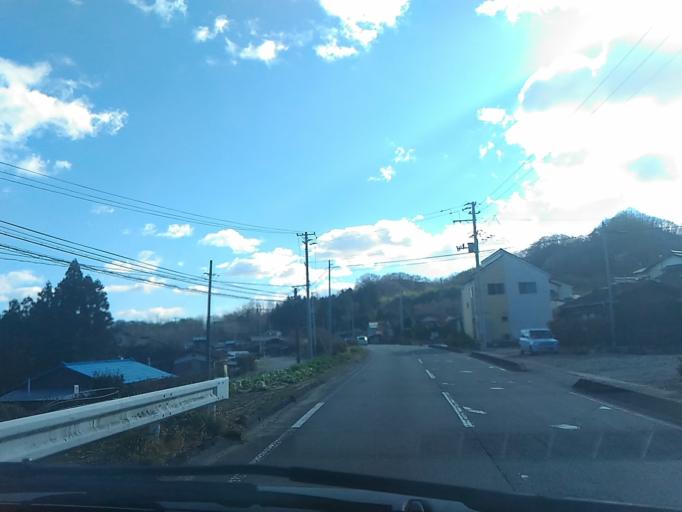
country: JP
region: Fukushima
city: Iwaki
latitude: 37.0109
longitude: 140.8258
